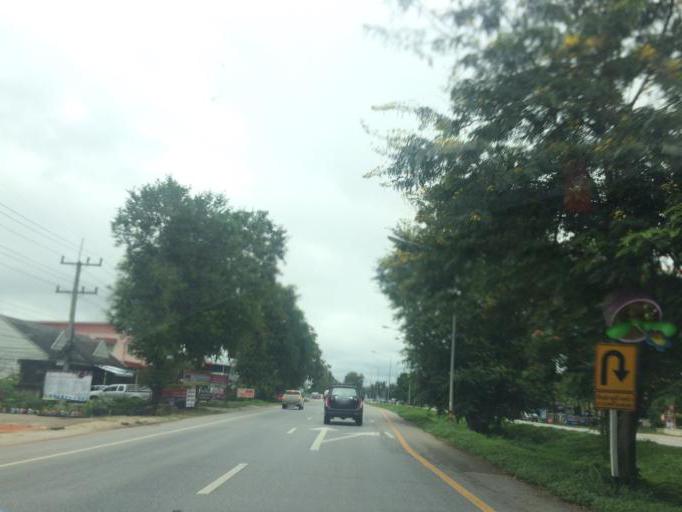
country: TH
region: Chiang Rai
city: Mae Lao
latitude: 19.7765
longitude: 99.7403
